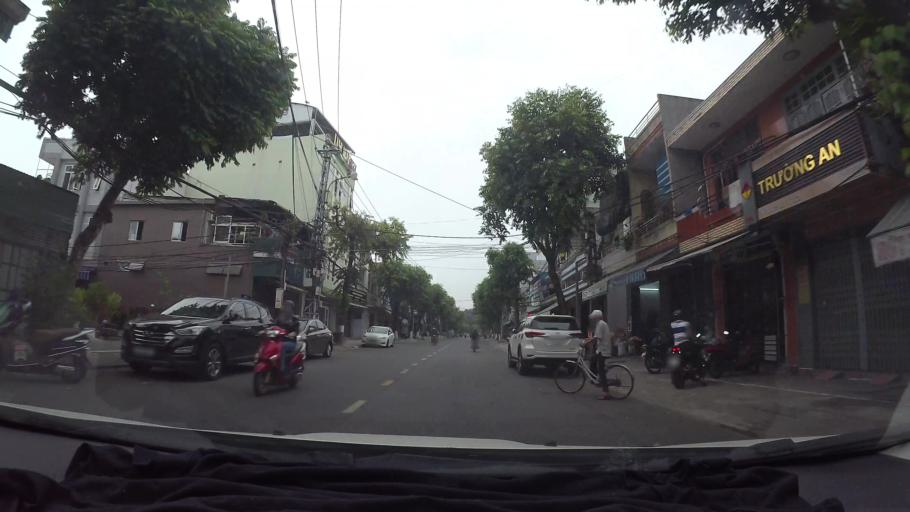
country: VN
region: Da Nang
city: Cam Le
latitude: 16.0300
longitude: 108.2226
